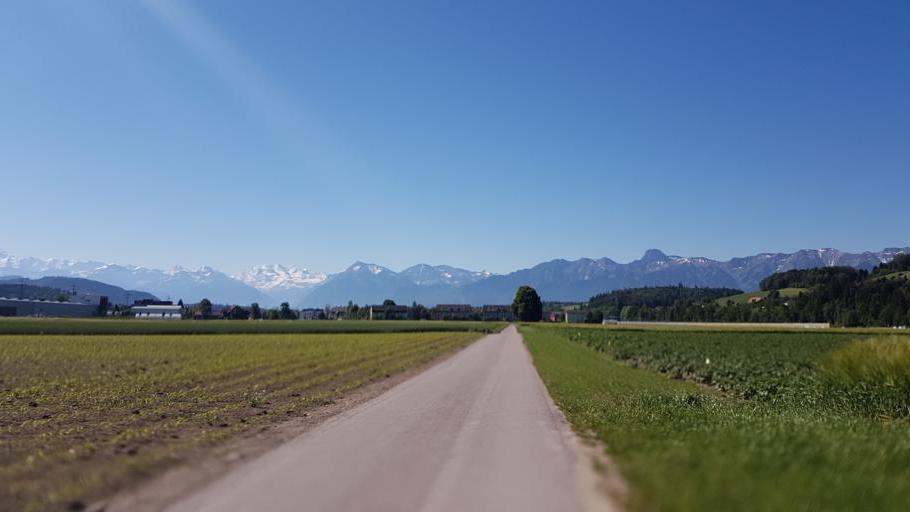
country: CH
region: Bern
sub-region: Bern-Mittelland District
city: Niederwichtrach
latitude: 46.8454
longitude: 7.5624
